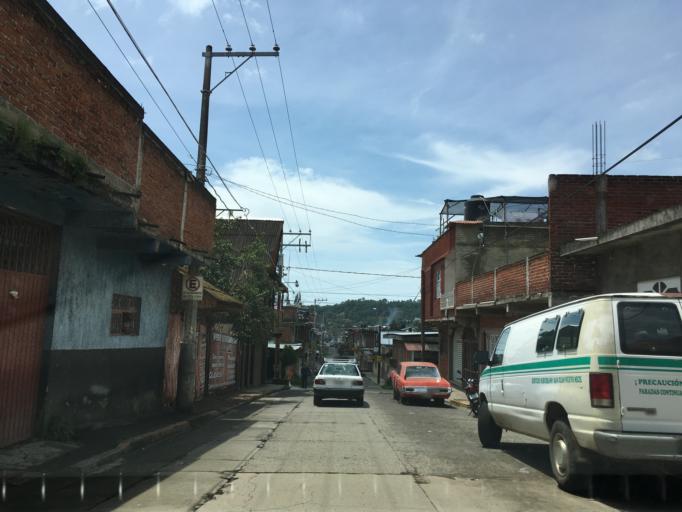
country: MX
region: Michoacan
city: Nuevo San Juan Parangaricutiro
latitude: 19.4215
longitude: -102.1333
